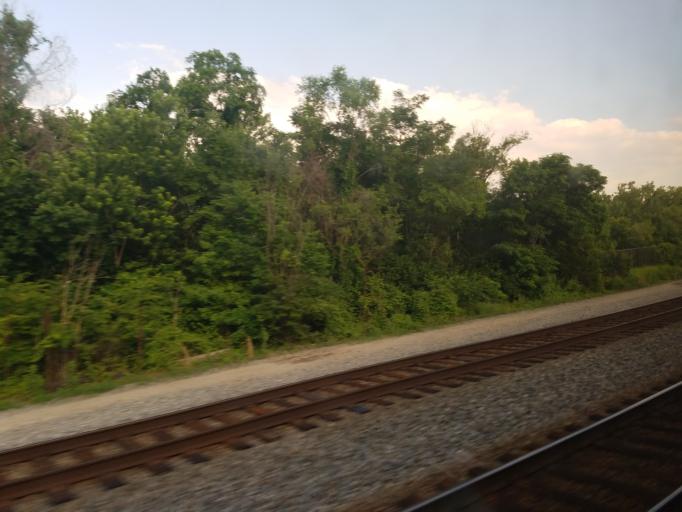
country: US
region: Virginia
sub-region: City of Alexandria
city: Alexandria
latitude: 38.8465
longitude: -77.0506
